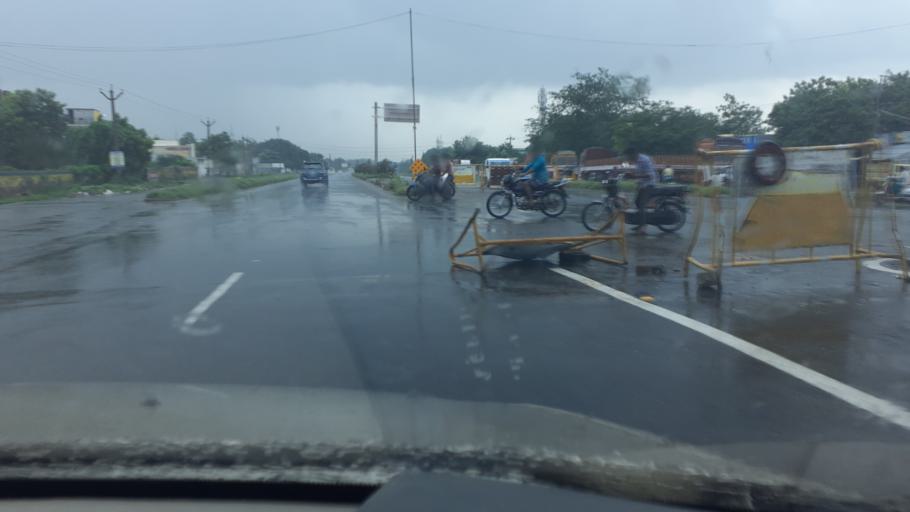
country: IN
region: Tamil Nadu
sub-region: Virudhunagar
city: Virudunagar
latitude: 9.5974
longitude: 77.9496
